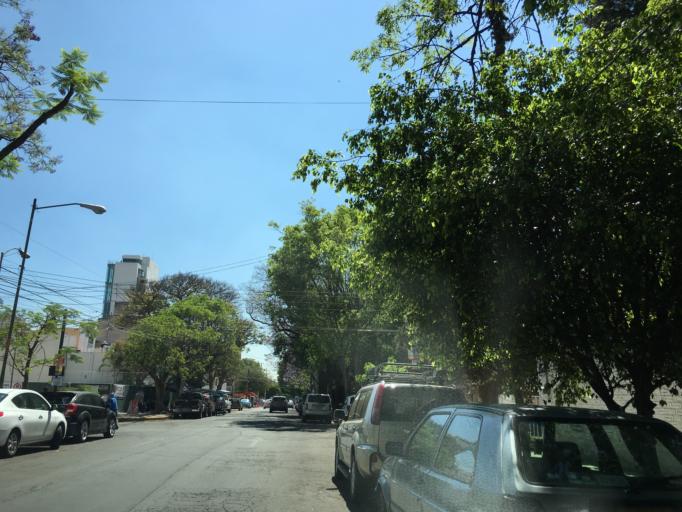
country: MX
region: Jalisco
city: Guadalajara
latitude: 20.6713
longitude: -103.3752
